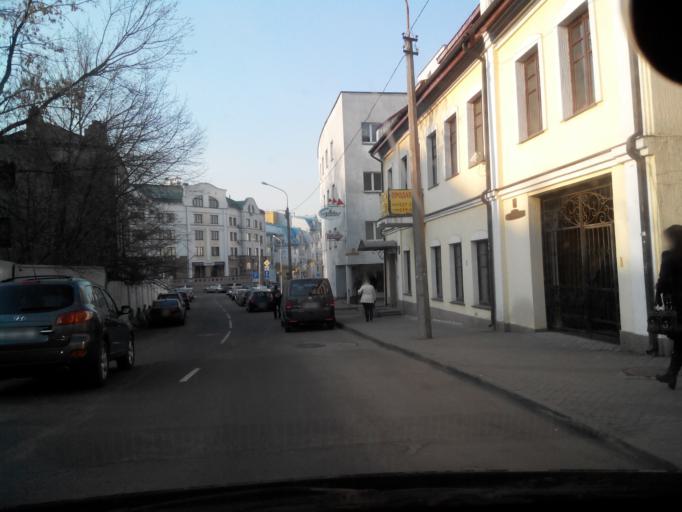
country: BY
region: Minsk
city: Minsk
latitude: 53.9061
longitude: 27.5474
